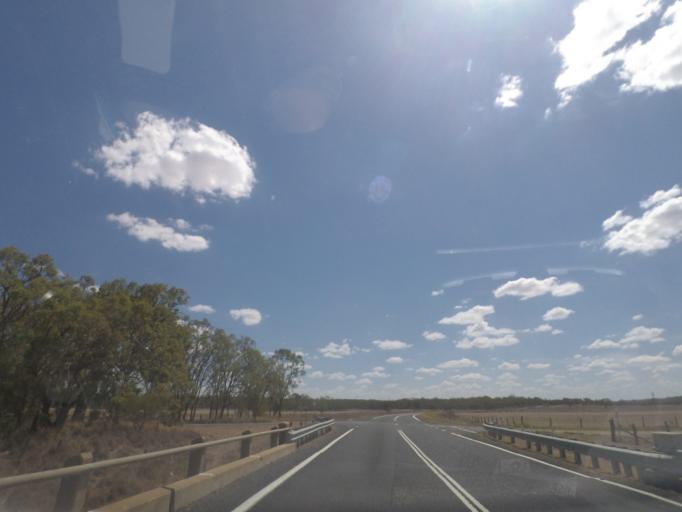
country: AU
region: Queensland
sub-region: Southern Downs
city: Warwick
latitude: -28.1832
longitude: 151.8169
